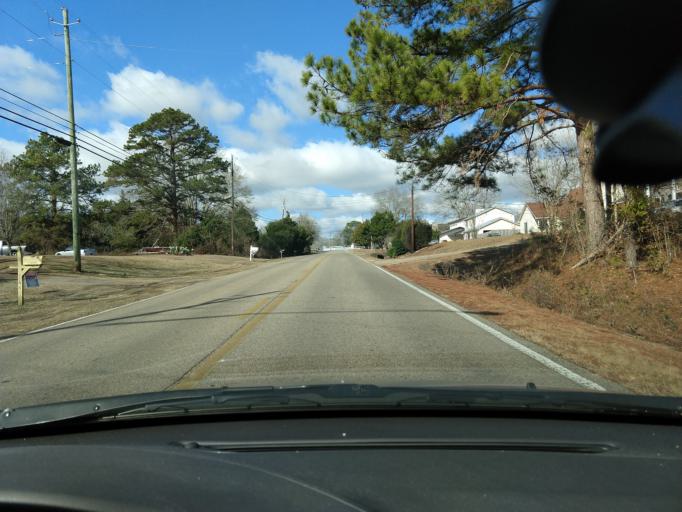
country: US
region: Alabama
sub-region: Coffee County
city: Enterprise
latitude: 31.3232
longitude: -85.8814
